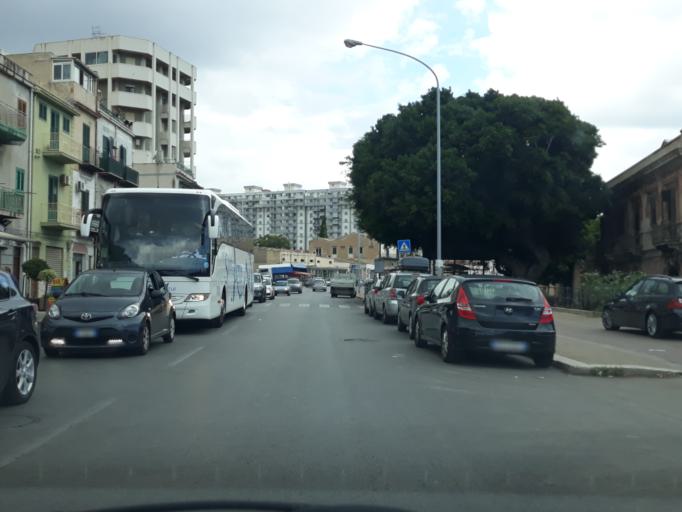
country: IT
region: Sicily
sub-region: Palermo
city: Ciaculli
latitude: 38.1067
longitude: 13.3846
